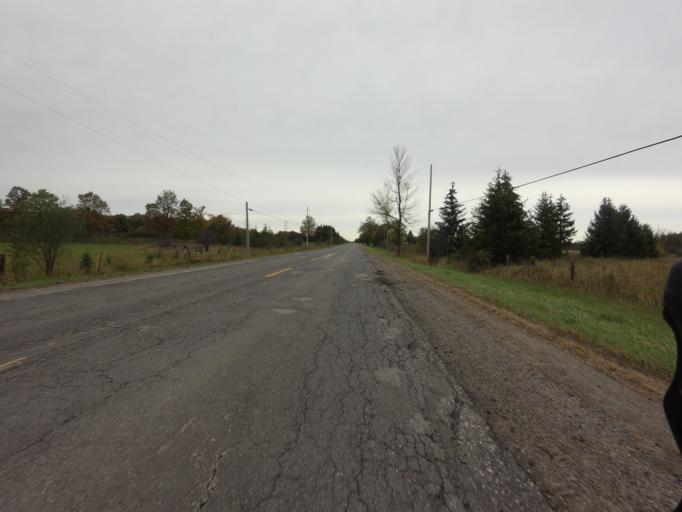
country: CA
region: Ontario
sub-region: Lanark County
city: Smiths Falls
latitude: 44.8720
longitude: -75.8114
